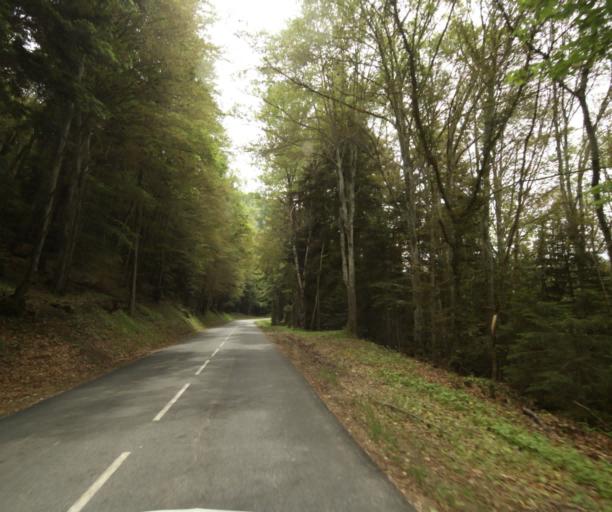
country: FR
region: Rhone-Alpes
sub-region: Departement de la Haute-Savoie
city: Perrignier
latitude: 46.2718
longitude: 6.4524
